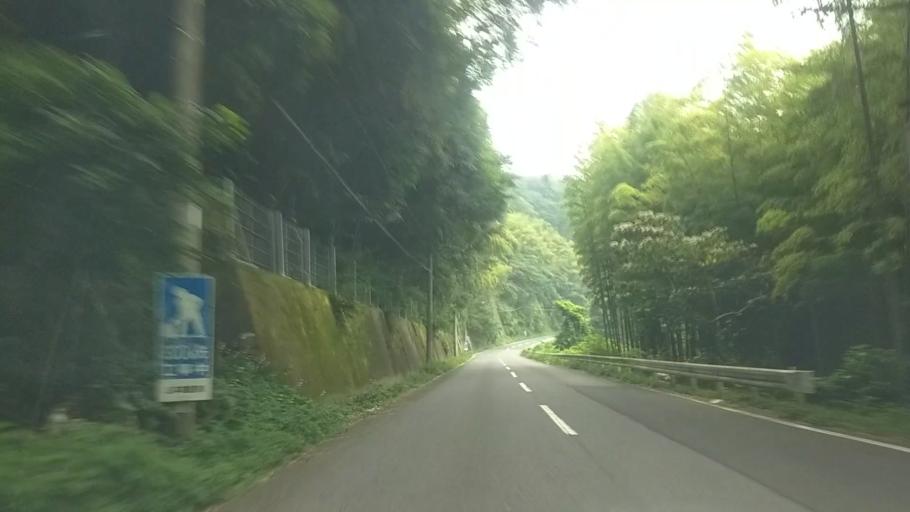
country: JP
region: Chiba
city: Katsuura
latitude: 35.2443
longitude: 140.2420
